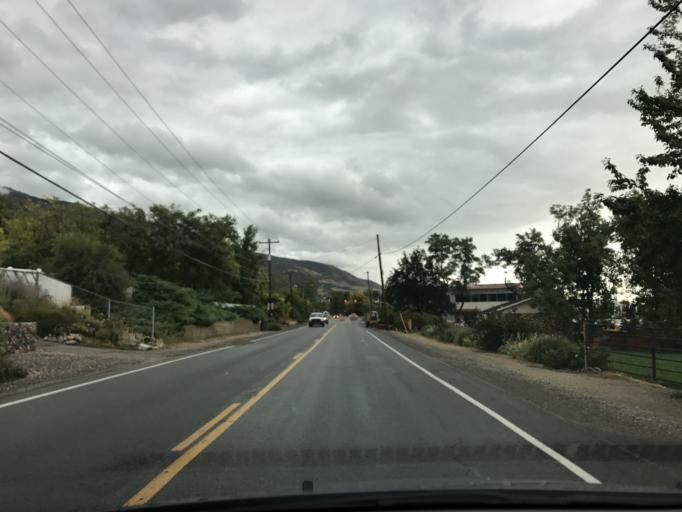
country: US
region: Utah
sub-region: Davis County
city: Farmington
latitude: 40.9931
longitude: -111.8947
